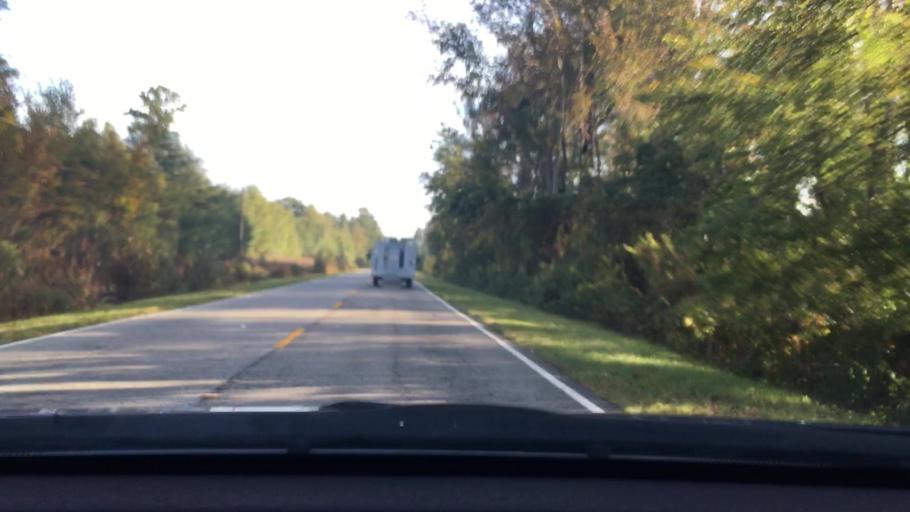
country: US
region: South Carolina
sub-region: Sumter County
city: East Sumter
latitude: 34.0433
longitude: -80.2585
